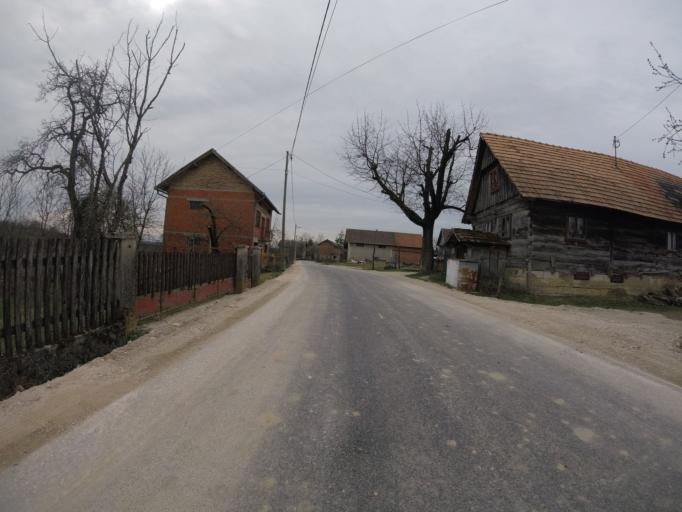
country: HR
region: Grad Zagreb
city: Strmec
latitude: 45.6094
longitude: 15.9108
